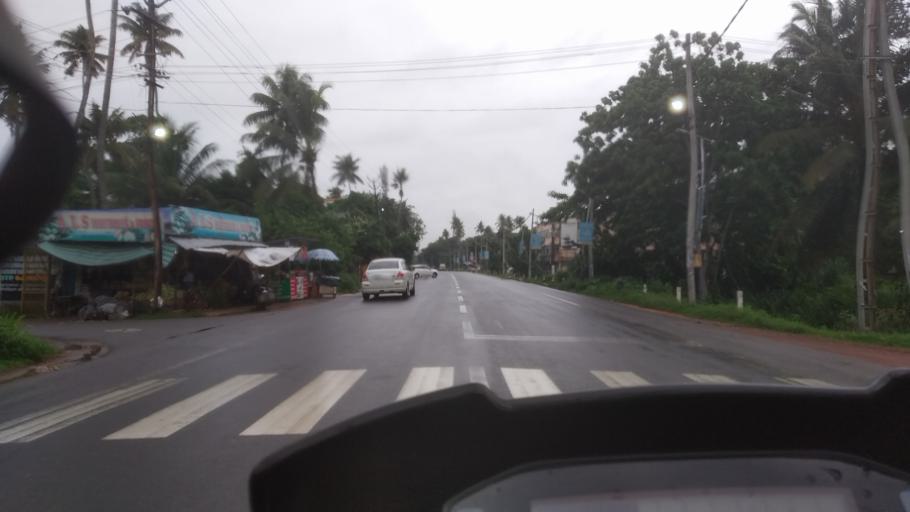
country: IN
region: Kerala
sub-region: Alappuzha
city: Kayankulam
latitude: 9.1334
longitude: 76.5140
